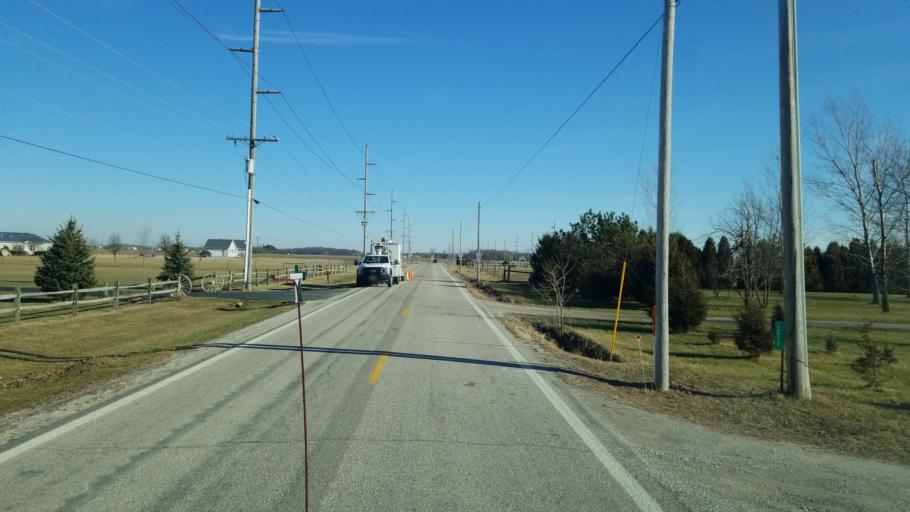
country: US
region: Ohio
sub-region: Sandusky County
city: Woodville
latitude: 41.4499
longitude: -83.4190
